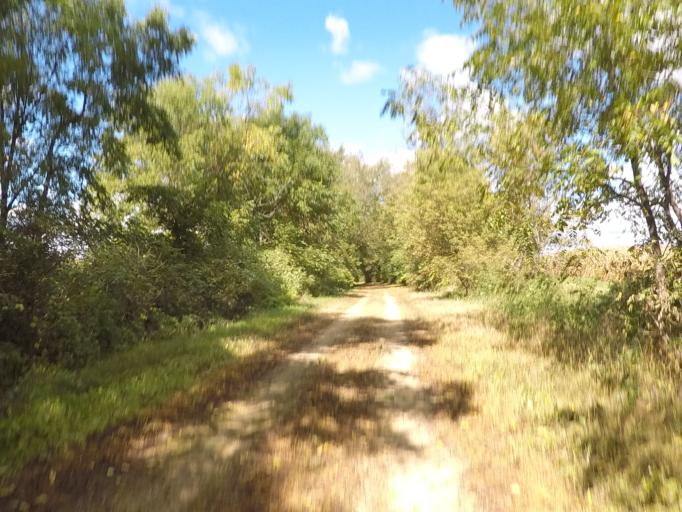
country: US
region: Wisconsin
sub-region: Richland County
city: Richland Center
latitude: 43.2899
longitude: -90.3246
